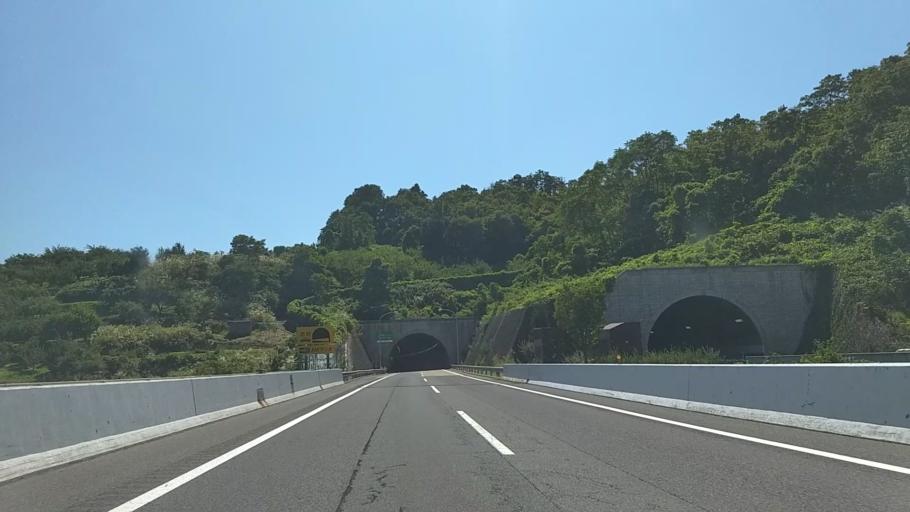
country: JP
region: Nagano
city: Nakano
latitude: 36.7542
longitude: 138.3133
